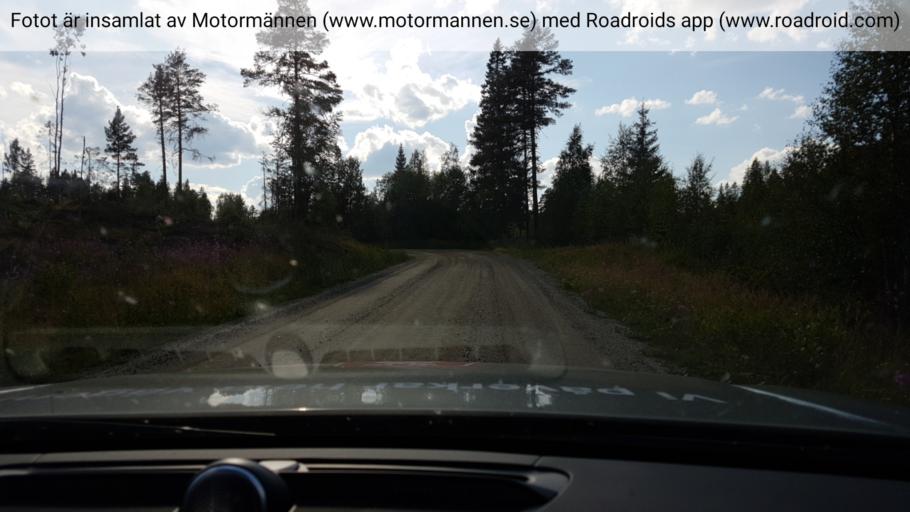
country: SE
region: Vaesternorrland
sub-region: Solleftea Kommun
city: As
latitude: 63.7783
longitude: 16.3166
